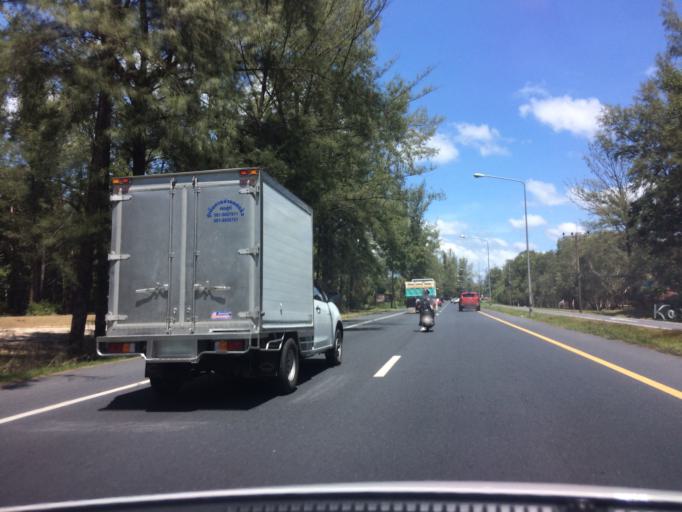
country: TH
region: Phuket
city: Thalang
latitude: 8.1921
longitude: 98.2889
